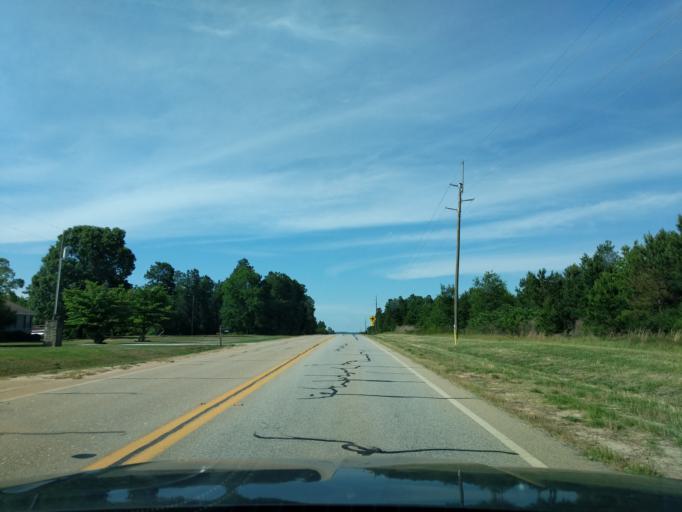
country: US
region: Georgia
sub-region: Jefferson County
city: Wrens
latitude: 33.2869
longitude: -82.3819
